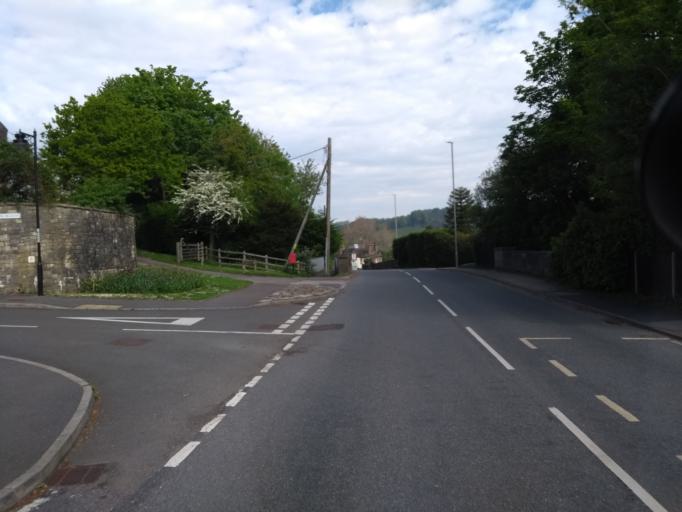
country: GB
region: England
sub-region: Dorset
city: Lyme Regis
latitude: 50.7316
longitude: -2.9485
